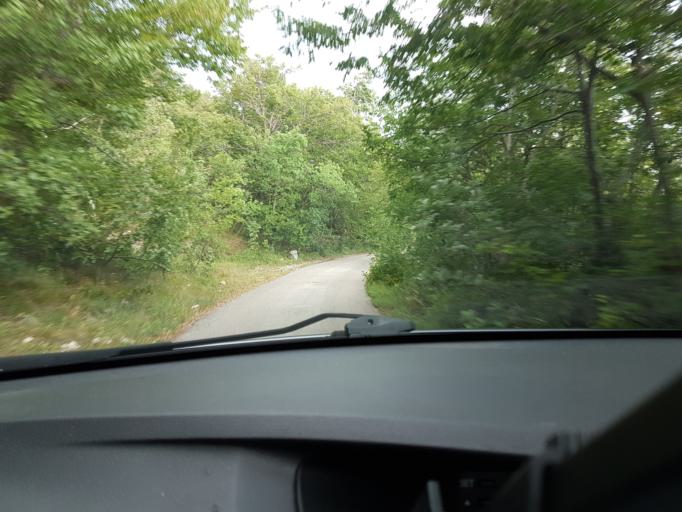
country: HR
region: Primorsko-Goranska
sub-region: Grad Crikvenica
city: Crikvenica
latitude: 45.2323
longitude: 14.7025
